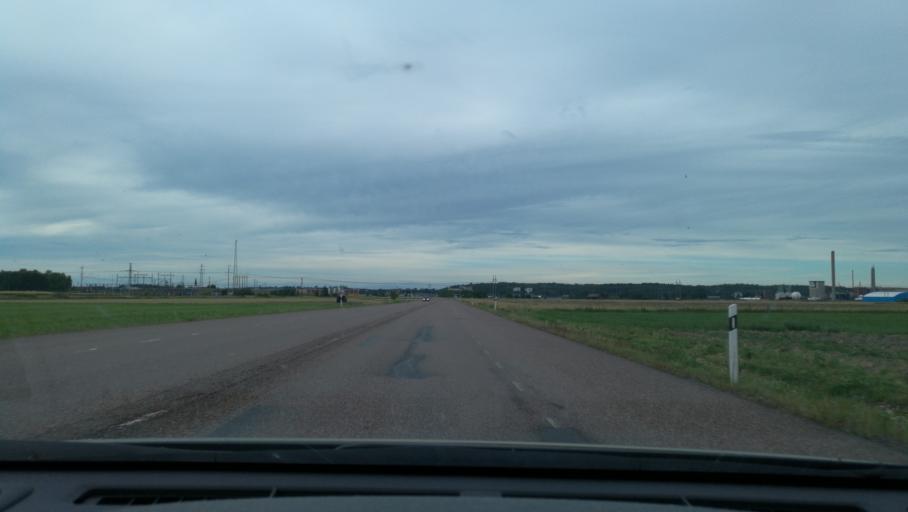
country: SE
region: Vaestmanland
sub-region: Kopings Kommun
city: Koping
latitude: 59.4899
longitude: 15.9877
